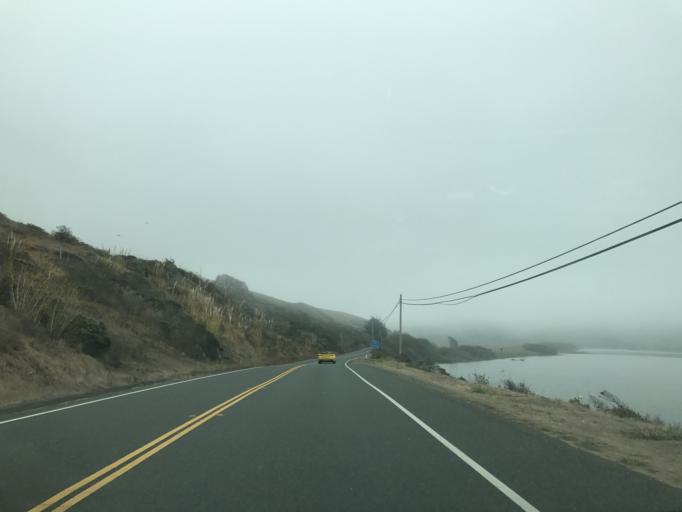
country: US
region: California
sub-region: Sonoma County
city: Monte Rio
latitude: 38.4458
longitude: -123.1121
